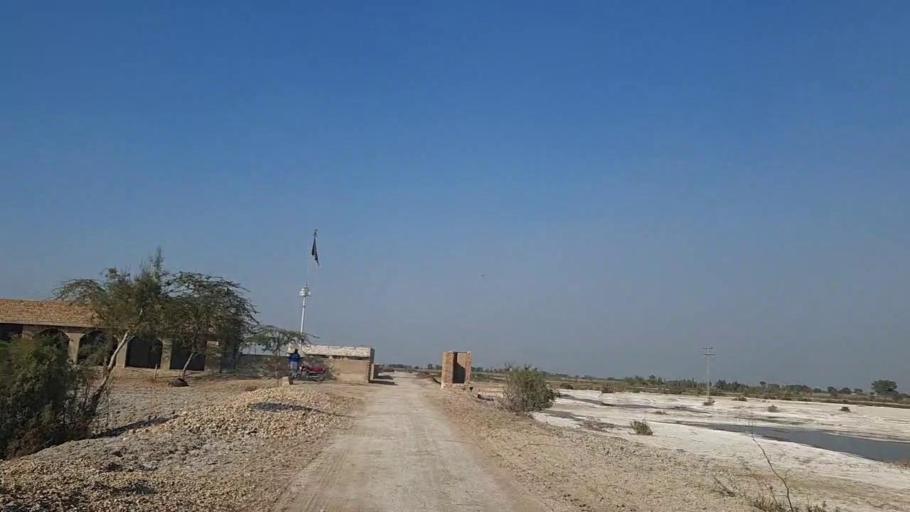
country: PK
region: Sindh
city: Daur
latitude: 26.3183
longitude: 68.1911
